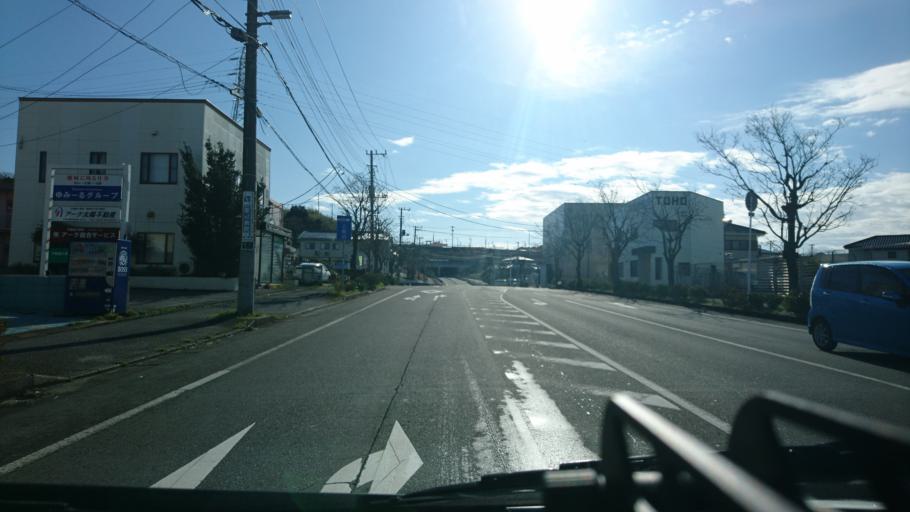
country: JP
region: Chiba
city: Kisarazu
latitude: 35.3675
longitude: 139.9290
